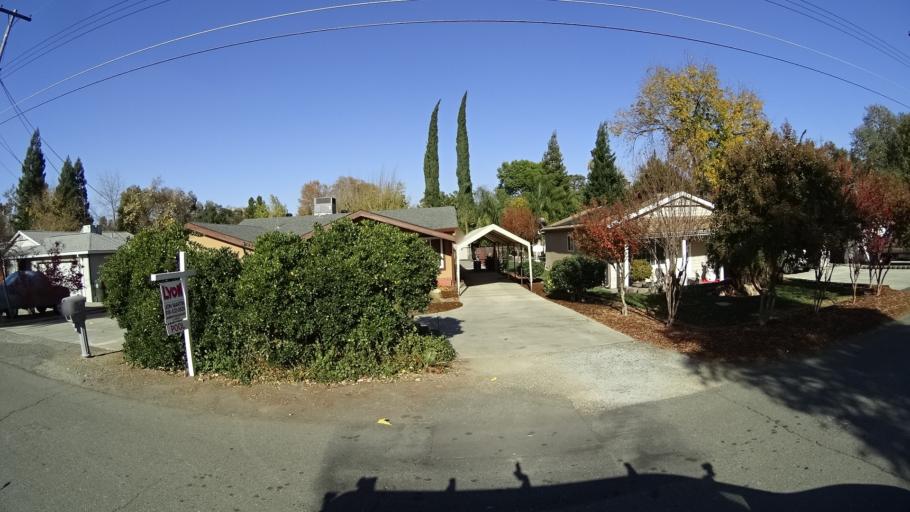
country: US
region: California
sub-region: Sacramento County
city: Citrus Heights
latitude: 38.7034
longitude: -121.2863
